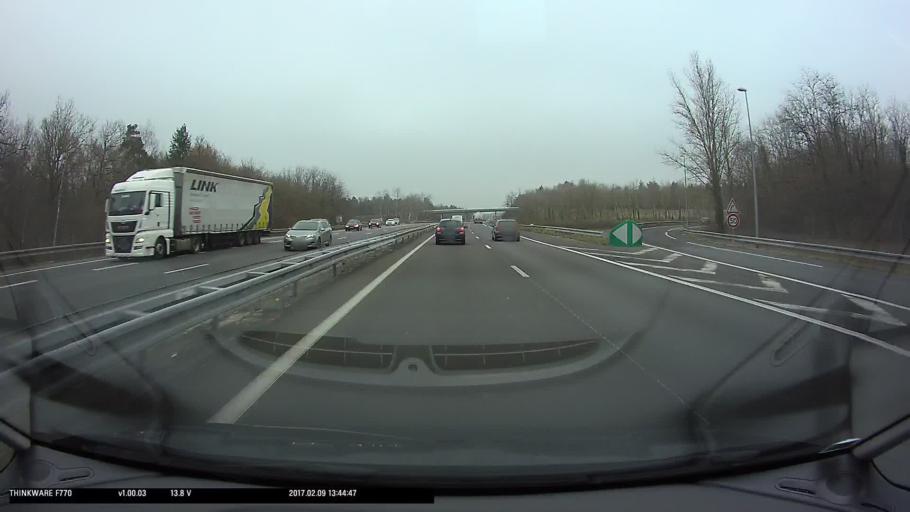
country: FR
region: Centre
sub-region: Departement du Loiret
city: Saint-Pryve-Saint-Mesmin
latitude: 47.8447
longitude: 1.8660
